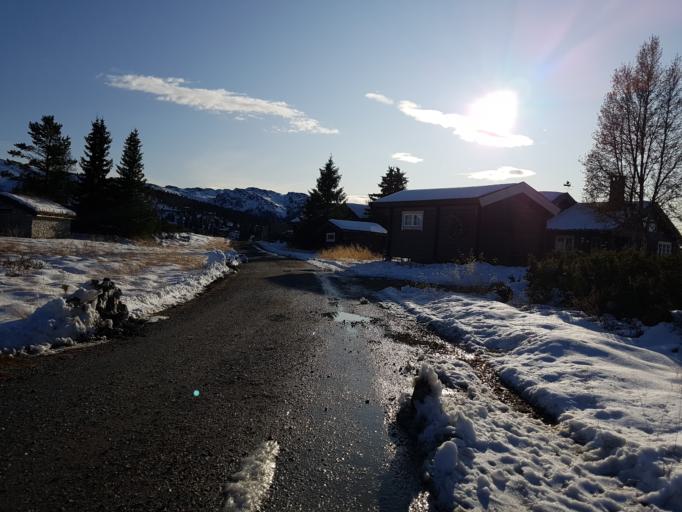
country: NO
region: Oppland
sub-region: Sel
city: Otta
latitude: 61.8129
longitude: 9.6815
